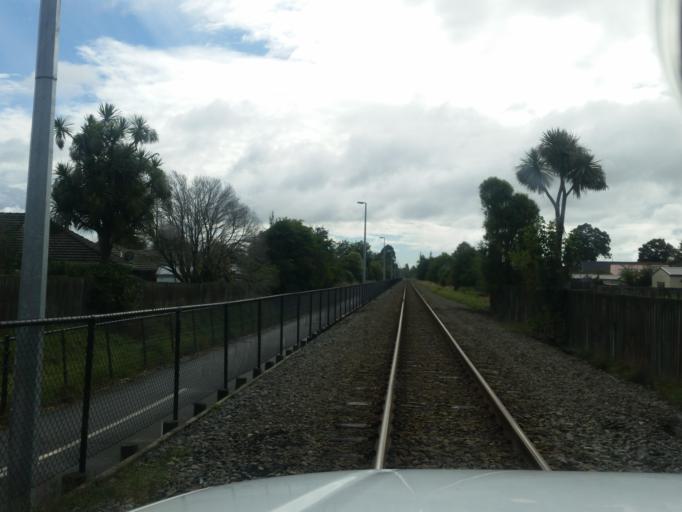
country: NZ
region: Canterbury
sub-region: Christchurch City
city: Christchurch
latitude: -43.4841
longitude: 172.6070
